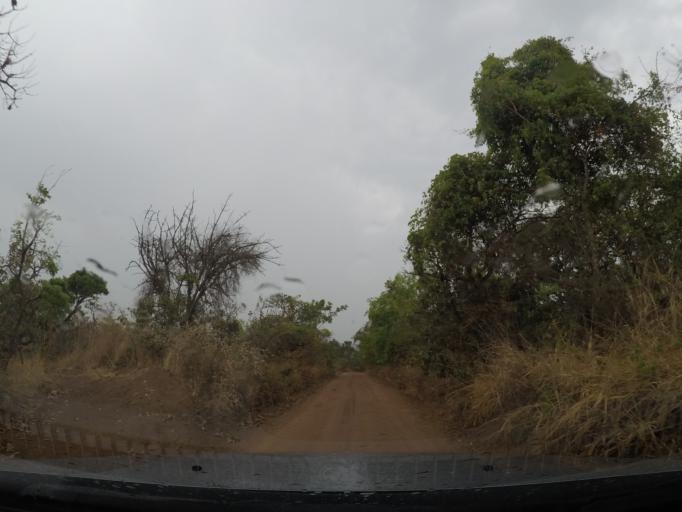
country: BR
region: Goias
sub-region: Pirenopolis
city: Pirenopolis
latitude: -15.8256
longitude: -48.8824
